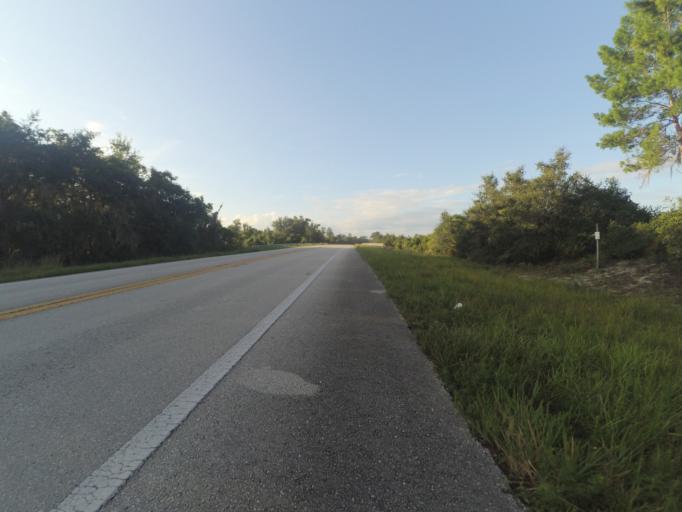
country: US
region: Florida
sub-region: Lake County
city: Astor
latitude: 29.2405
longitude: -81.6472
